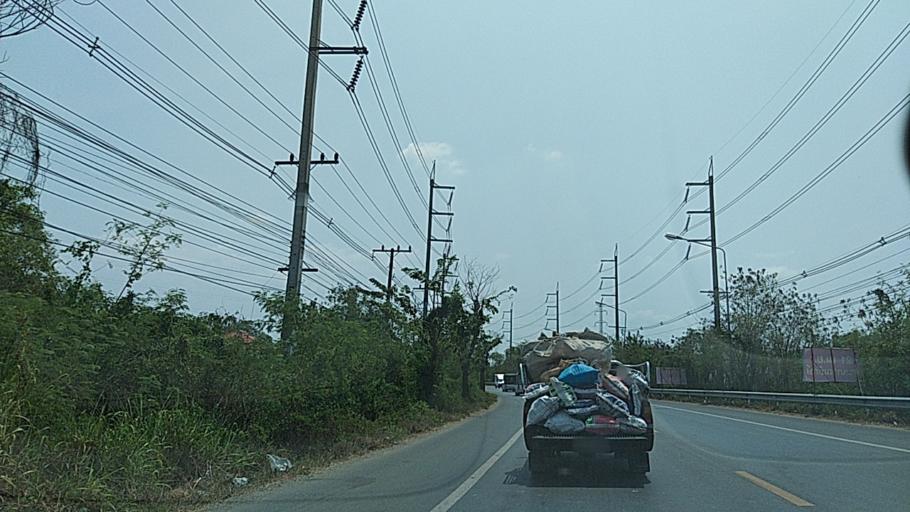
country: TH
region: Chachoengsao
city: Bang Nam Priao
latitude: 13.7926
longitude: 101.0526
